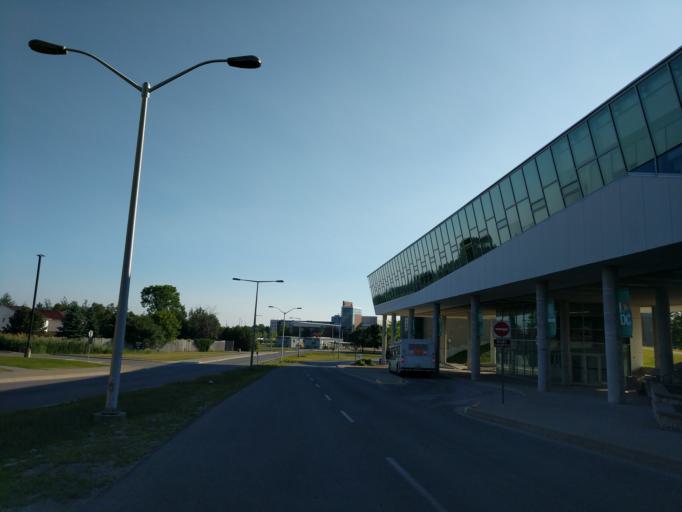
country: CA
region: Ontario
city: Oshawa
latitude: 43.9446
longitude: -78.8935
